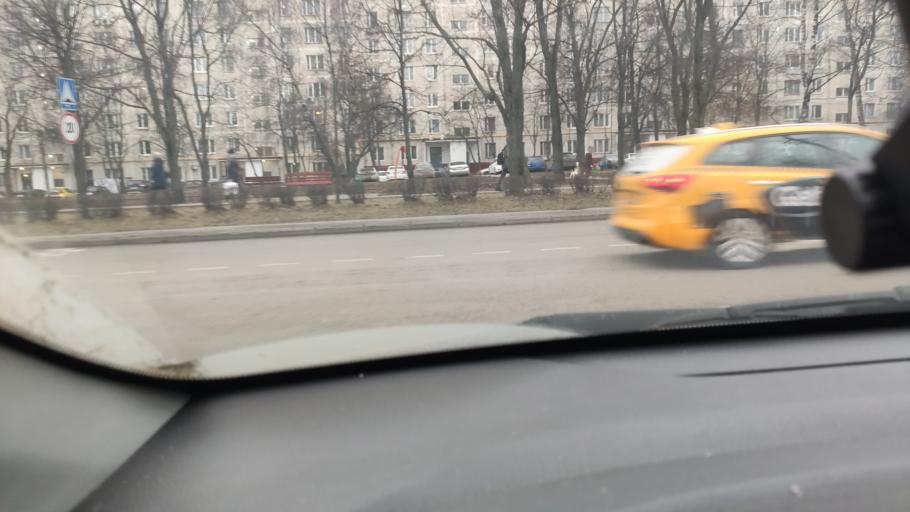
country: RU
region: Moscow
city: Chertanovo Yuzhnoye
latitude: 55.5948
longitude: 37.6082
